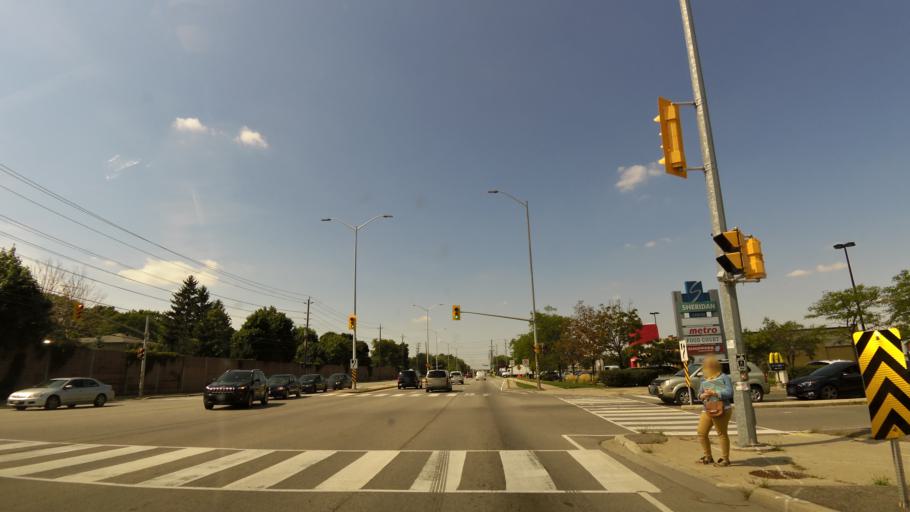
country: CA
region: Ontario
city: Mississauga
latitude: 43.5289
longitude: -79.6545
